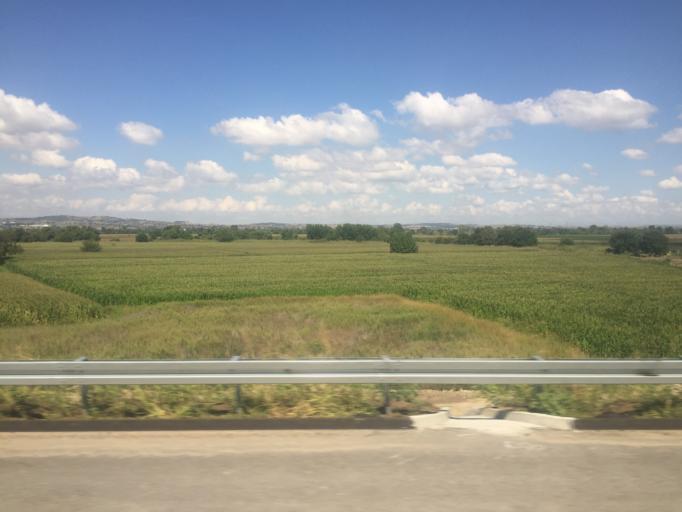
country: TR
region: Balikesir
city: Gobel
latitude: 40.0235
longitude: 28.2072
